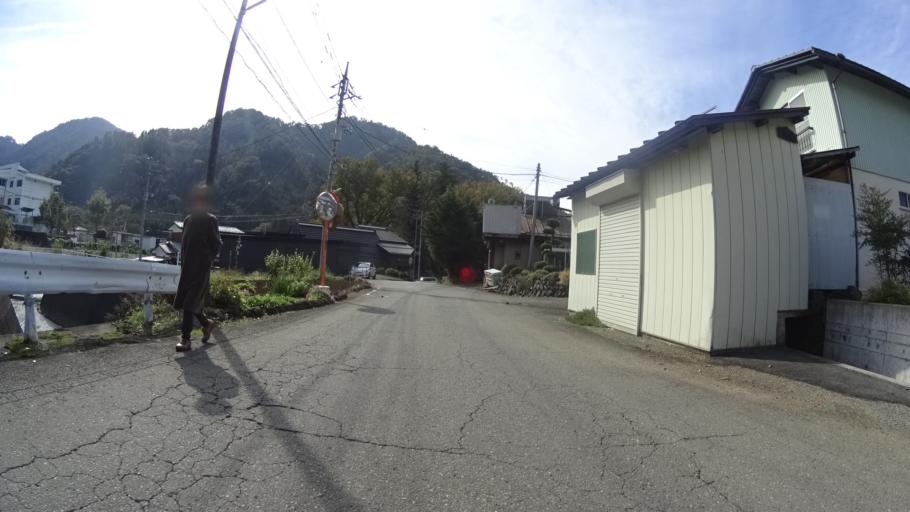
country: JP
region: Yamanashi
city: Otsuki
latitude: 35.5643
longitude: 138.9736
